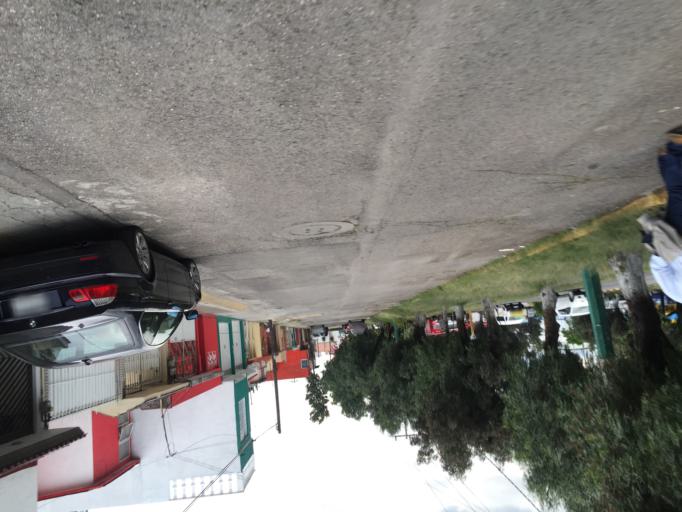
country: MX
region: Mexico
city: Cuautitlan Izcalli
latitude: 19.6546
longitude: -99.2096
